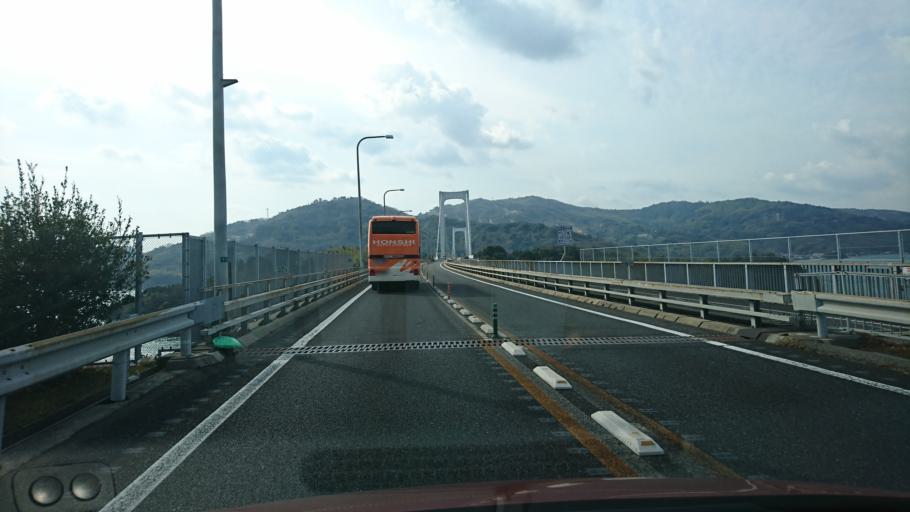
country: JP
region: Hiroshima
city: Innoshima
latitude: 34.1979
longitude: 133.0777
